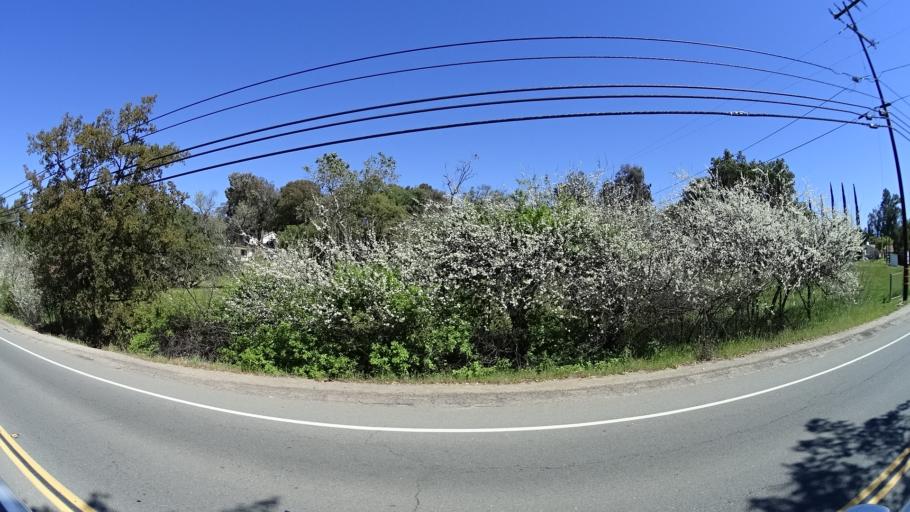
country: US
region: California
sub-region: San Diego County
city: Alpine
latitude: 32.8310
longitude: -116.7753
